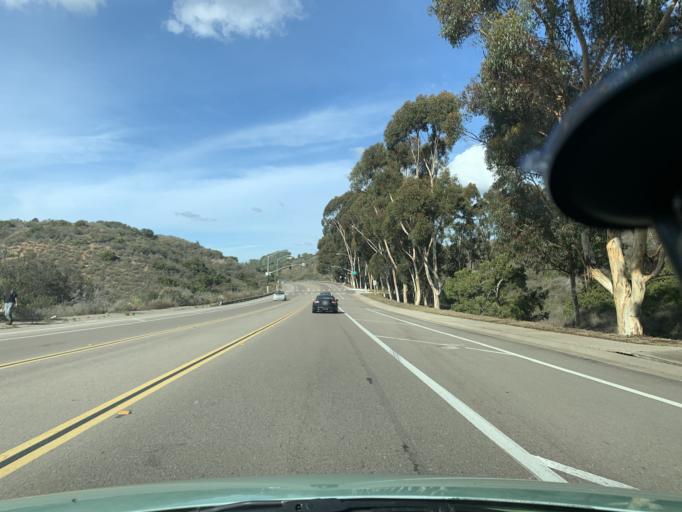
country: US
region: California
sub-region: San Diego County
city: San Diego
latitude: 32.7964
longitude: -117.1715
